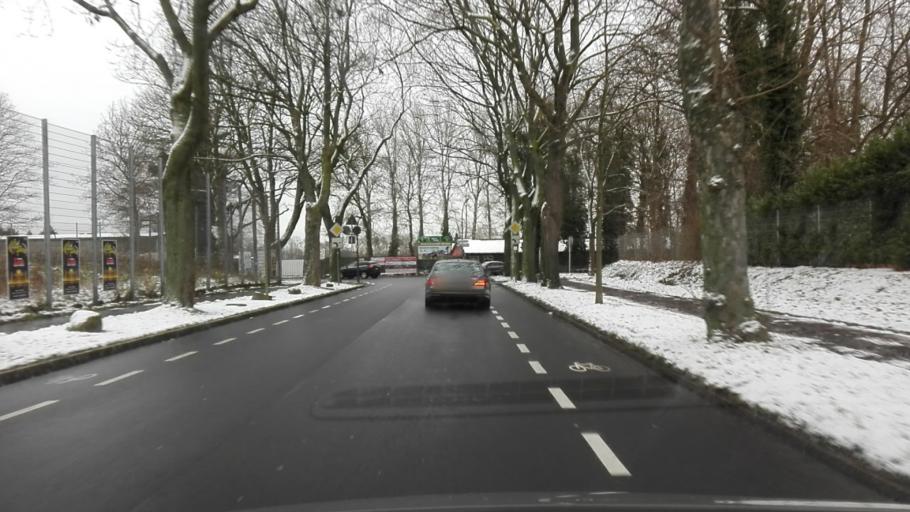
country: DE
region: North Rhine-Westphalia
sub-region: Regierungsbezirk Arnsberg
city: Dortmund
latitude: 51.5130
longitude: 7.5334
